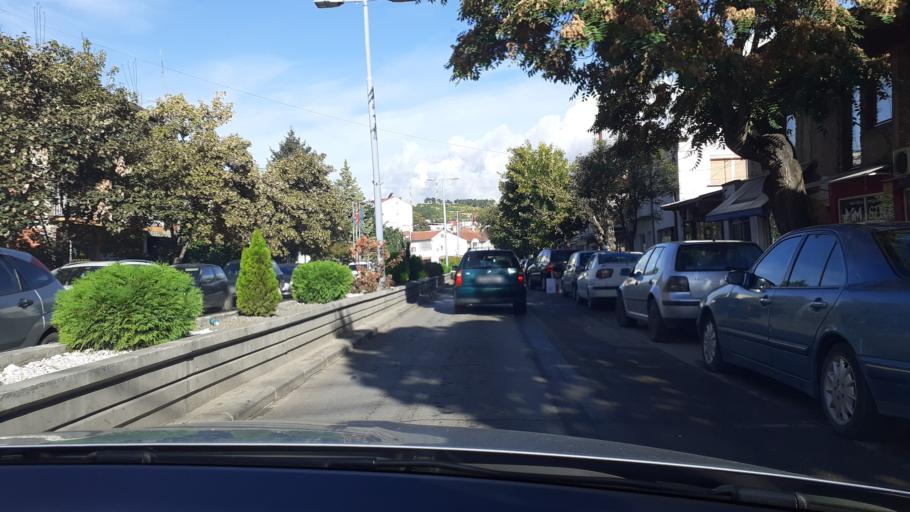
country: MK
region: Kocani
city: Kochani
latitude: 41.9139
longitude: 22.4147
